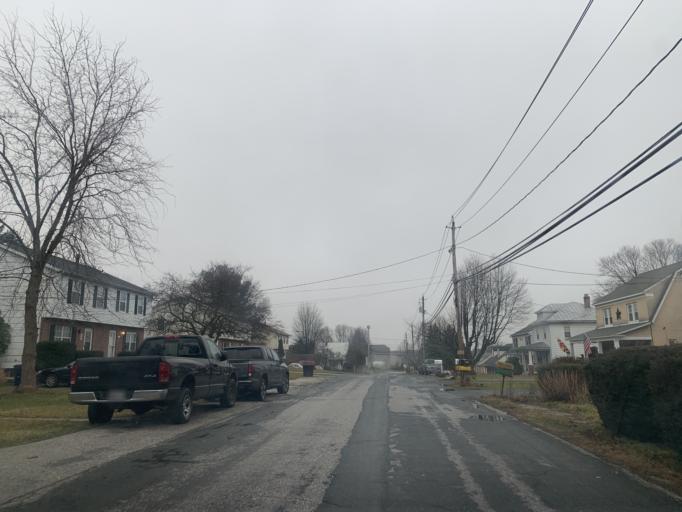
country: US
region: Maryland
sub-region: Carroll County
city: Westminster
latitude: 39.5602
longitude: -76.9716
